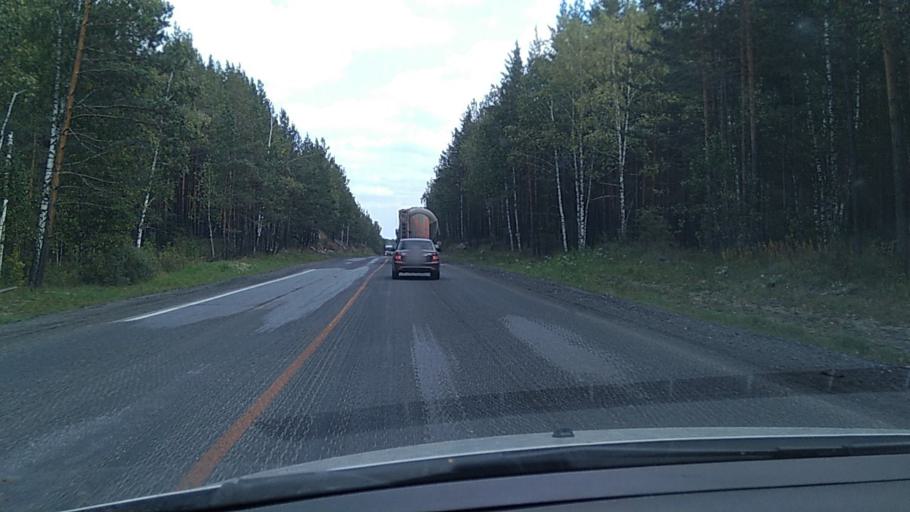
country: RU
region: Chelyabinsk
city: Miass
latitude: 54.9303
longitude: 60.1776
